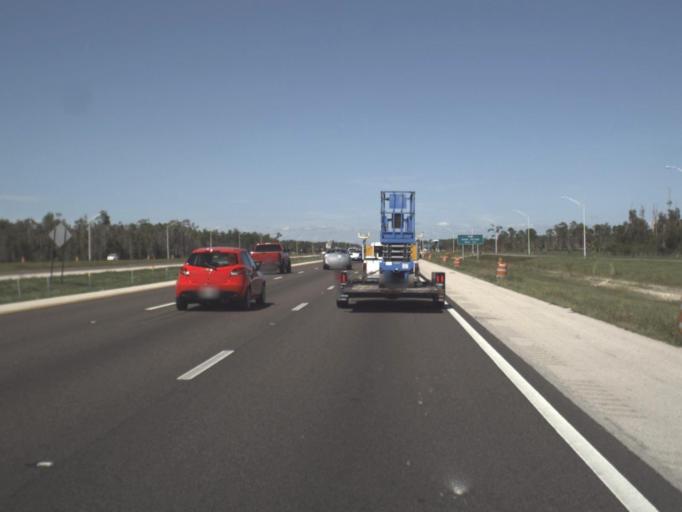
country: US
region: Florida
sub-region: Lee County
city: Three Oaks
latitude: 26.5148
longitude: -81.7945
